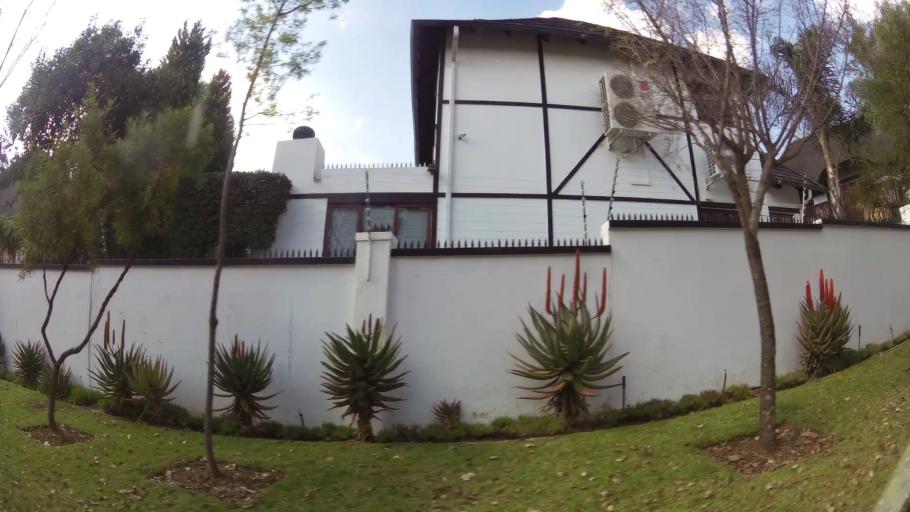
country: ZA
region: Gauteng
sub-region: City of Johannesburg Metropolitan Municipality
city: Midrand
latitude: -26.0242
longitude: 28.0752
